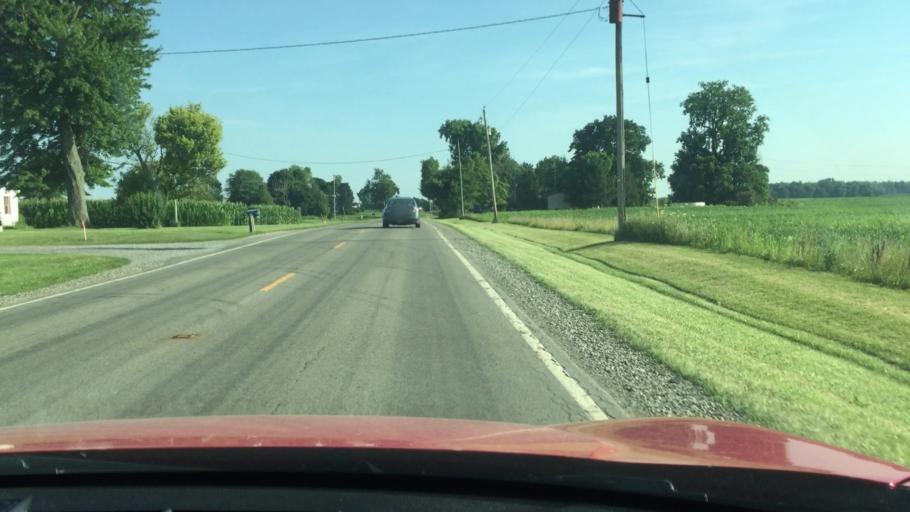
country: US
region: Ohio
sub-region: Hardin County
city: Ada
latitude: 40.6873
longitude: -83.8572
